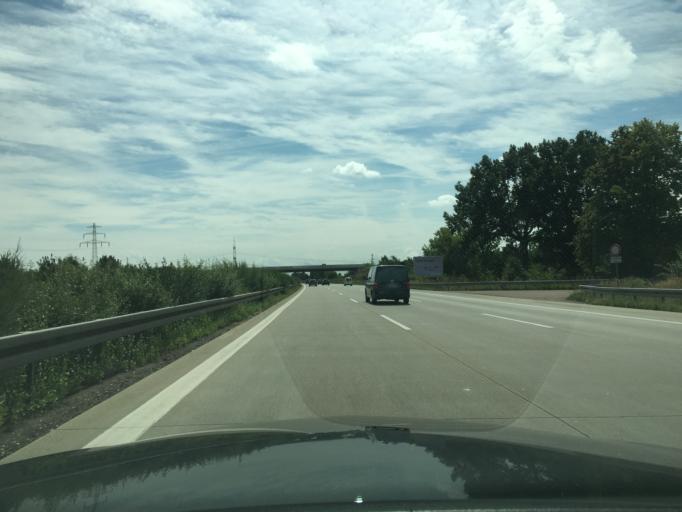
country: DE
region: Saxony-Anhalt
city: Landsberg
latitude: 51.5177
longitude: 12.1972
